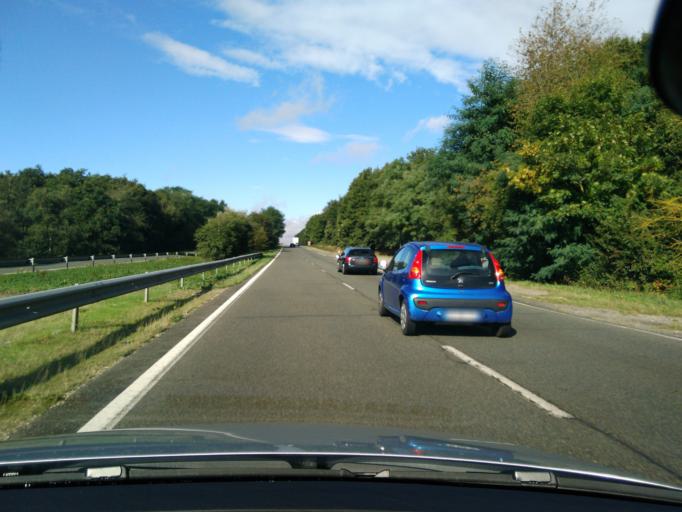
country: FR
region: Haute-Normandie
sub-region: Departement de l'Eure
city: Saint-Germain-sur-Avre
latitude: 48.7509
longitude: 1.2621
